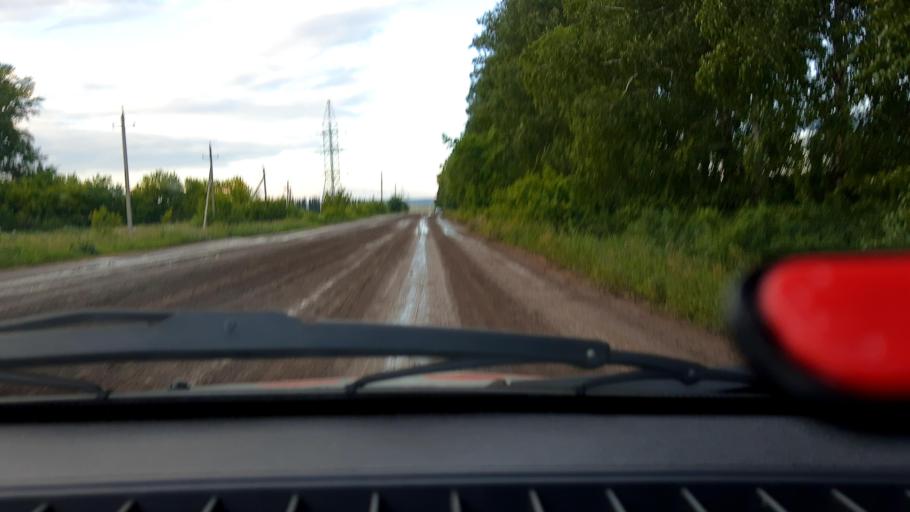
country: RU
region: Bashkortostan
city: Tolbazy
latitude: 54.1928
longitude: 55.8808
